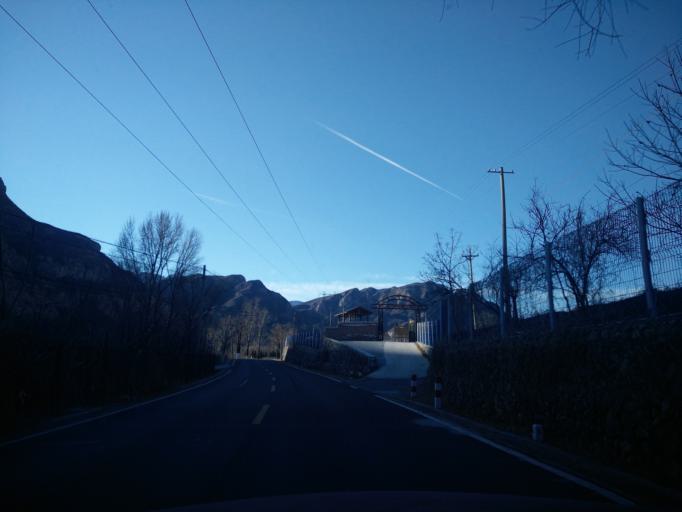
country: CN
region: Beijing
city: Yanchi
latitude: 40.0240
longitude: 115.8365
